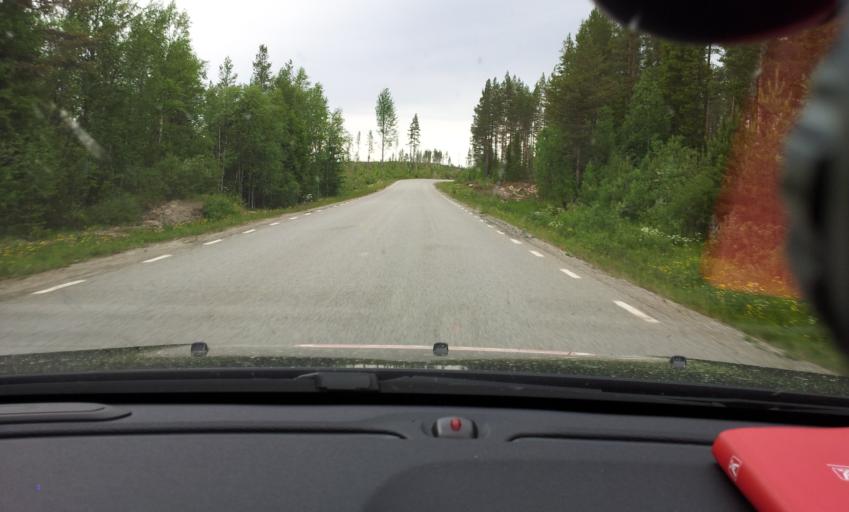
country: SE
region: Jaemtland
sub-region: Bergs Kommun
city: Hoverberg
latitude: 62.6884
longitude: 14.6341
